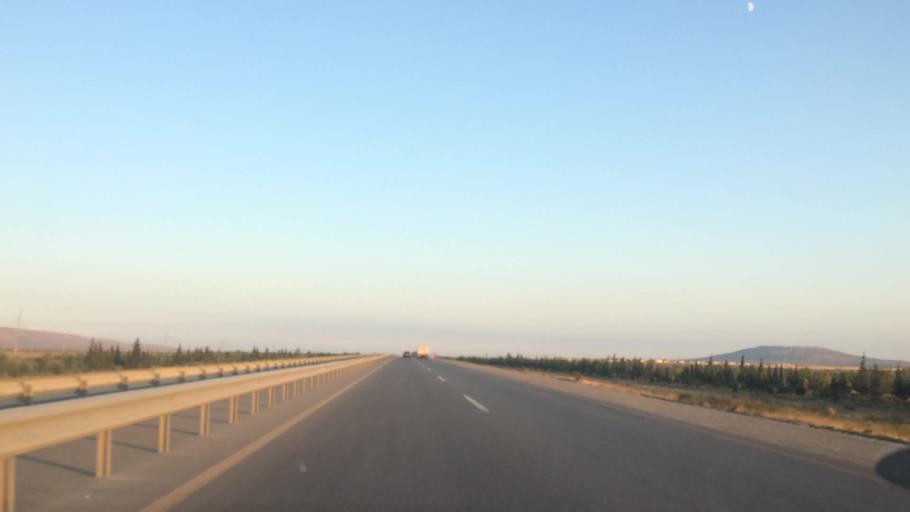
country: AZ
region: Baki
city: Qobustan
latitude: 39.9913
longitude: 49.1959
